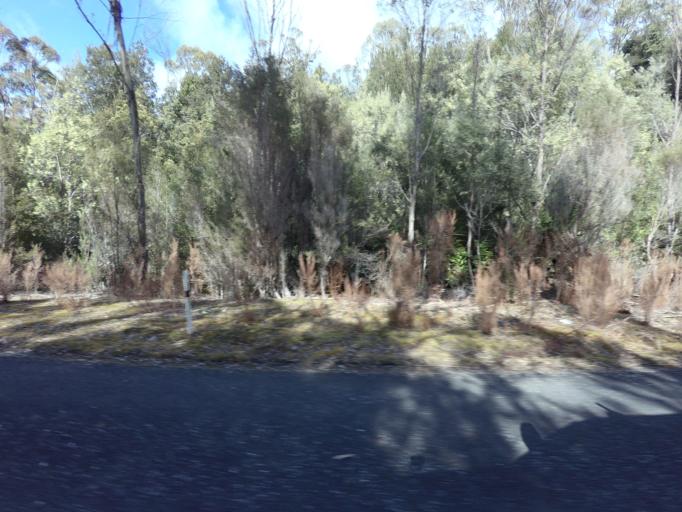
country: AU
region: Tasmania
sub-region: Huon Valley
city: Geeveston
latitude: -42.8138
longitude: 146.1016
